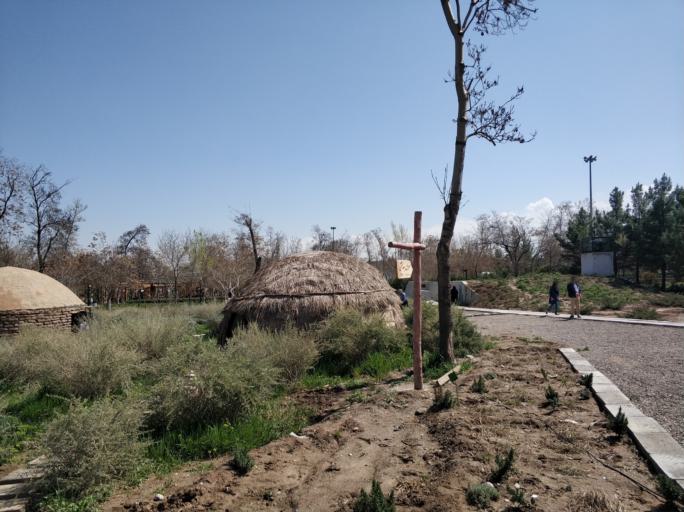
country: IR
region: Razavi Khorasan
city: Mashhad
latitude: 36.2523
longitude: 59.6082
